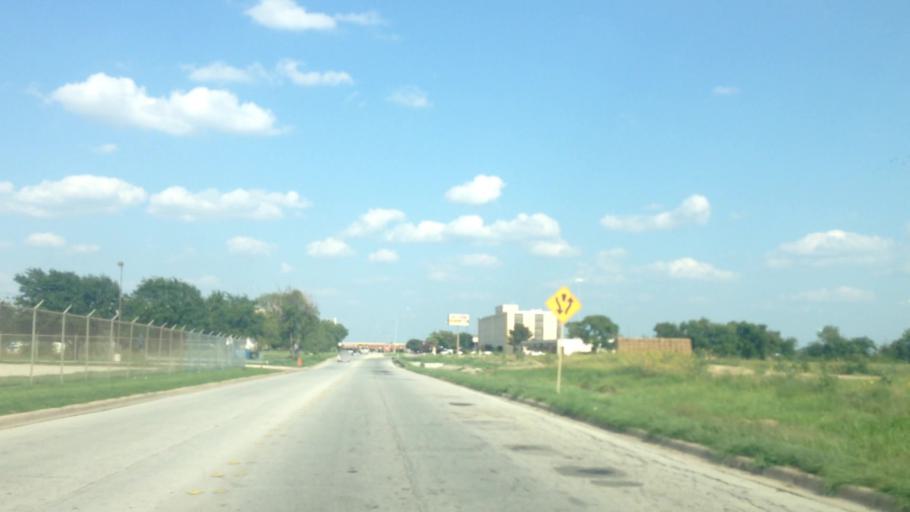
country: US
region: Texas
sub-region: Tarrant County
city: Blue Mound
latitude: 32.8245
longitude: -97.3196
